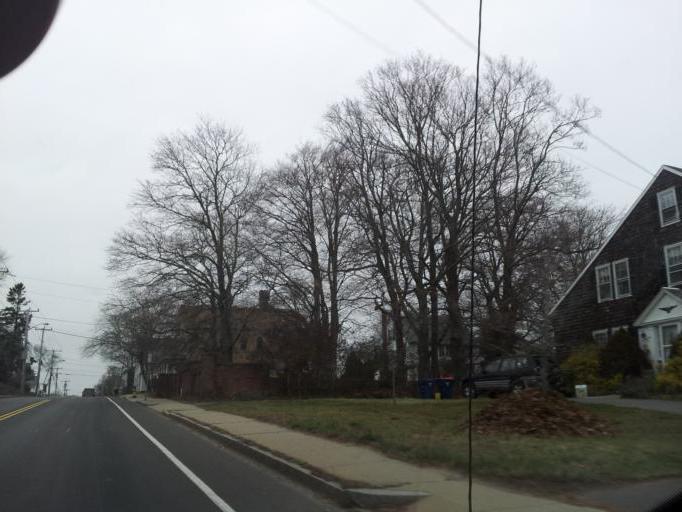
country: US
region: Massachusetts
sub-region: Plymouth County
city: Plymouth
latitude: 41.9498
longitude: -70.6533
